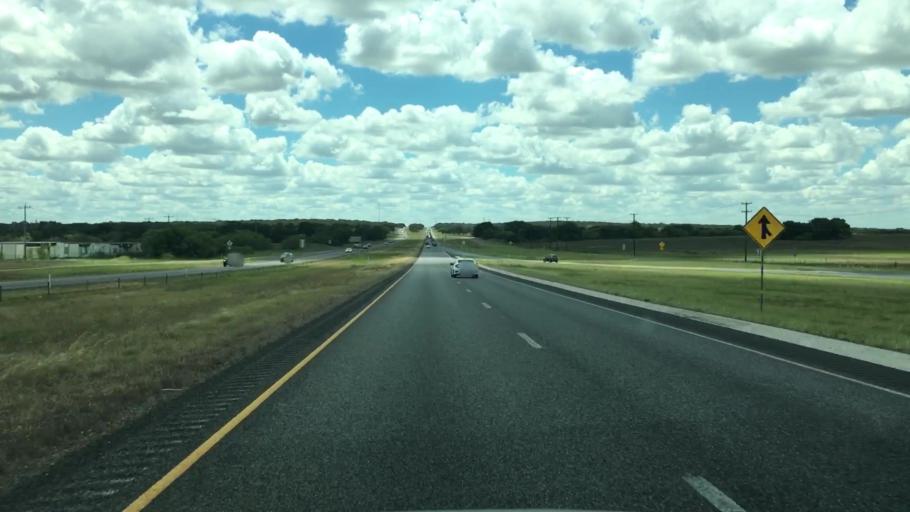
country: US
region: Texas
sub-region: Bexar County
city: Elmendorf
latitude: 29.2156
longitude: -98.4137
